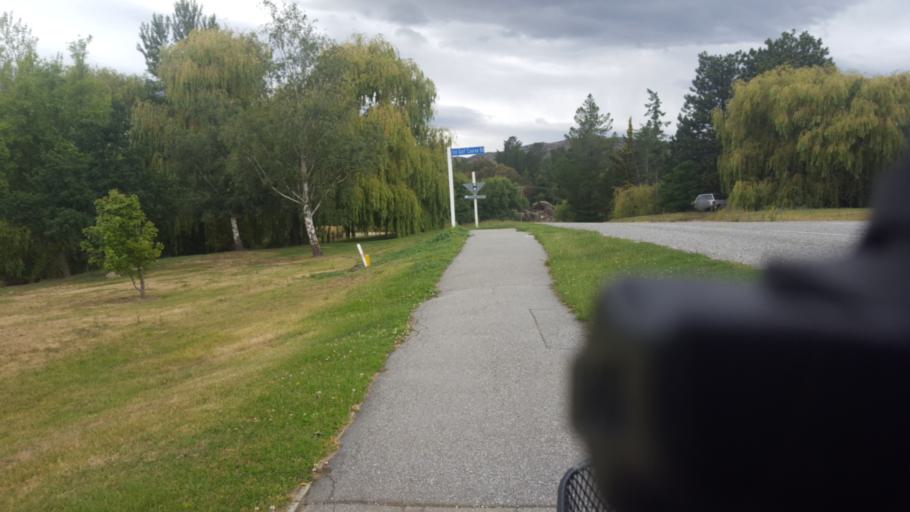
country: NZ
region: Otago
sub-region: Queenstown-Lakes District
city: Wanaka
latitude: -45.2638
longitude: 169.3774
